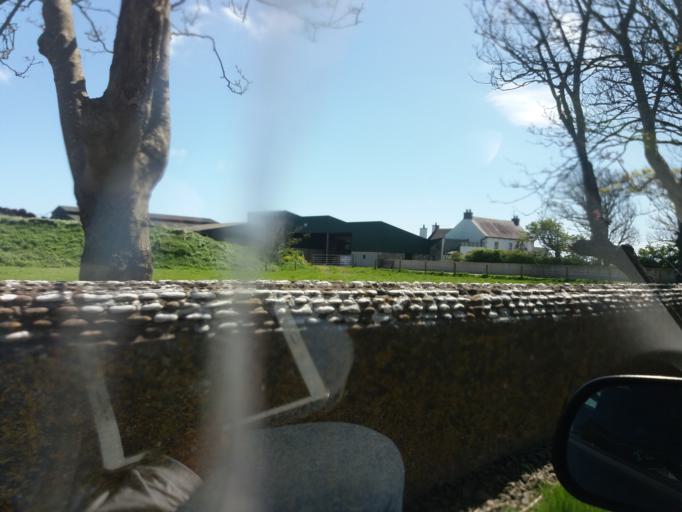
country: IE
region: Munster
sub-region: Waterford
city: Dunmore East
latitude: 52.1460
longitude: -6.9073
